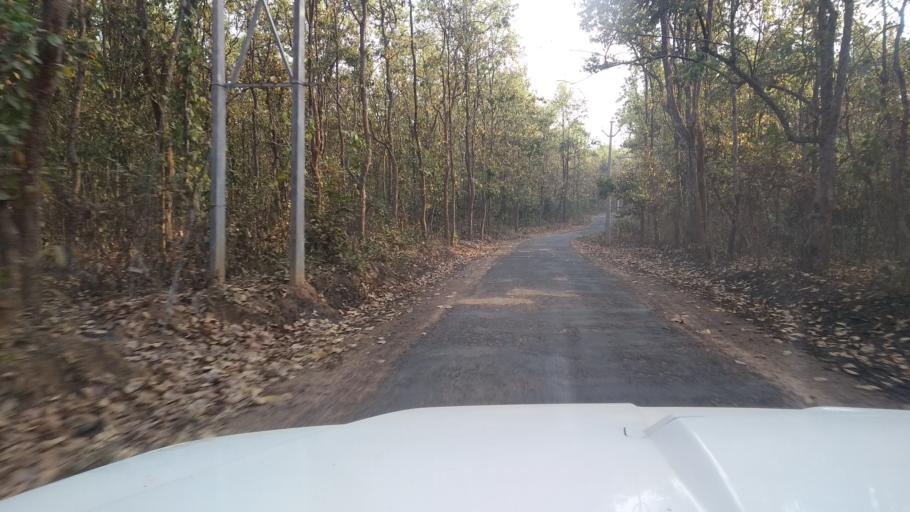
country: IN
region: Tripura
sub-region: West Tripura
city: Sonamura
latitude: 23.3352
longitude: 91.3133
